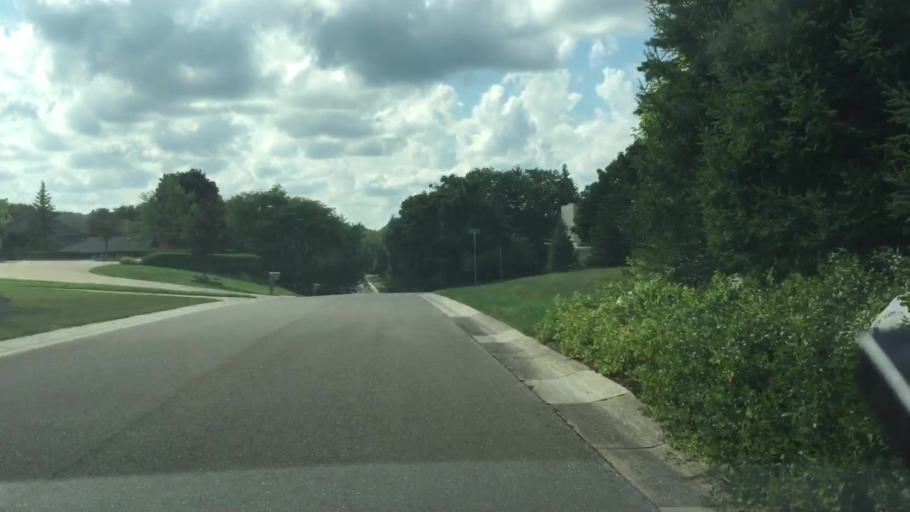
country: US
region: Michigan
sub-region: Oakland County
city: Sylvan Lake
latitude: 42.5739
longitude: -83.3128
